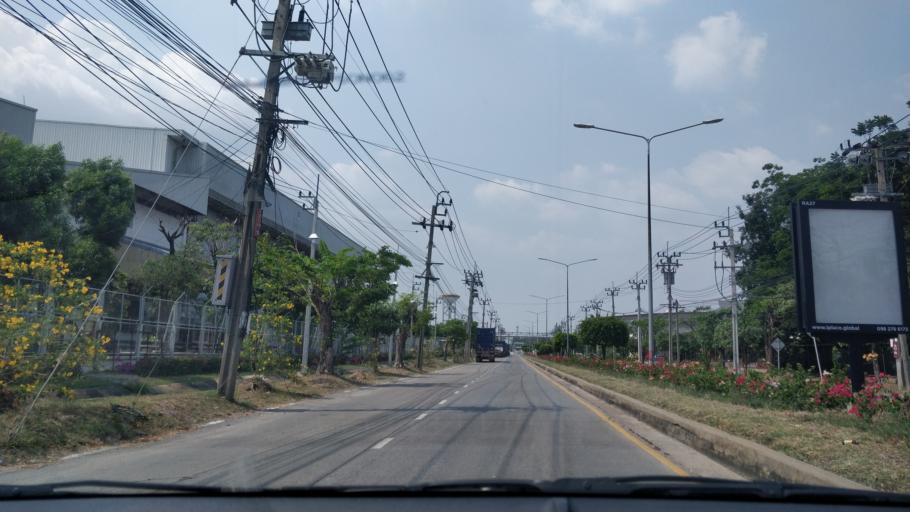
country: TH
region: Bangkok
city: Lat Krabang
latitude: 13.7642
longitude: 100.7833
